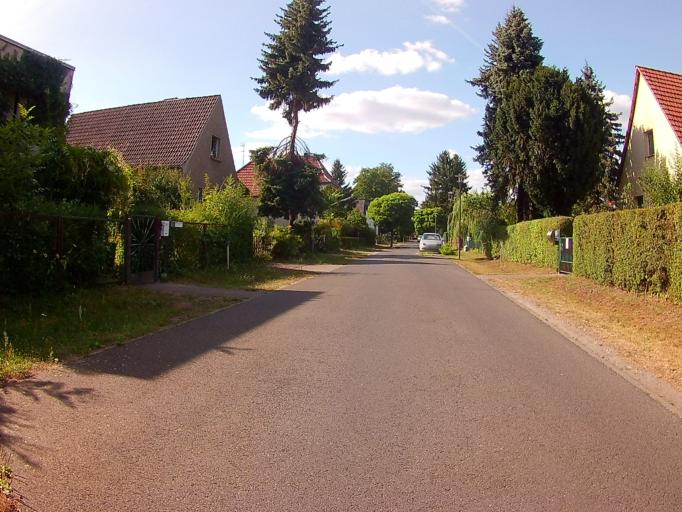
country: DE
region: Brandenburg
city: Zeuthen
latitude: 52.3651
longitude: 13.6121
